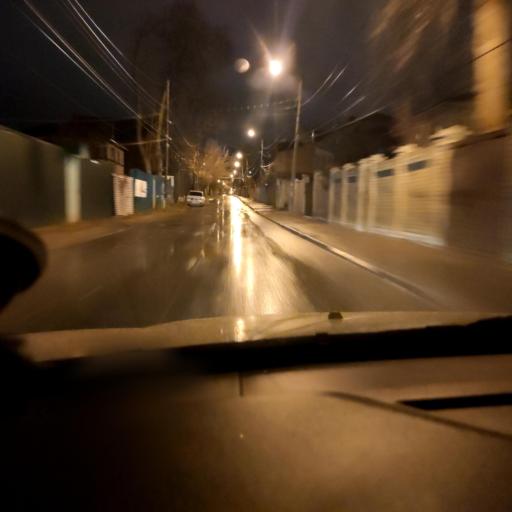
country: RU
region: Samara
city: Samara
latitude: 53.2563
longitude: 50.1866
